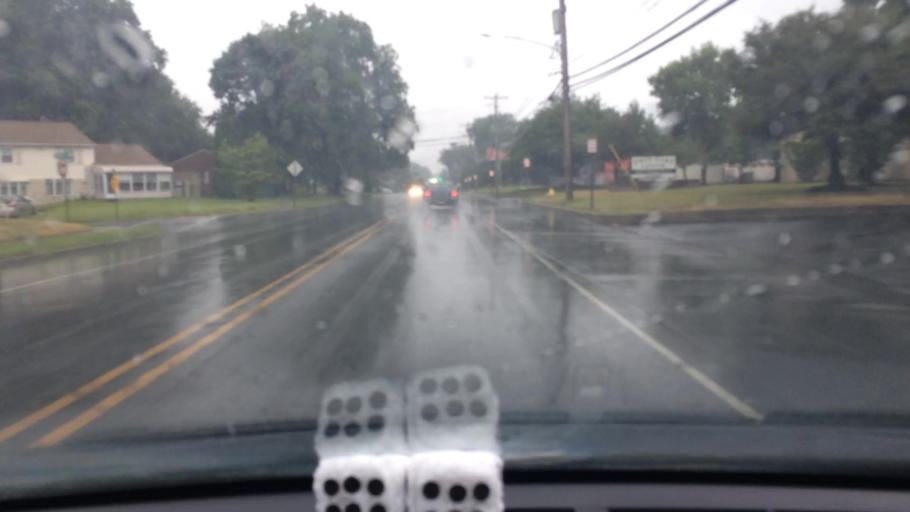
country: US
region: Pennsylvania
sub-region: Delaware County
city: Village Green-Green Ridge
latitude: 39.8485
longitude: -75.4259
